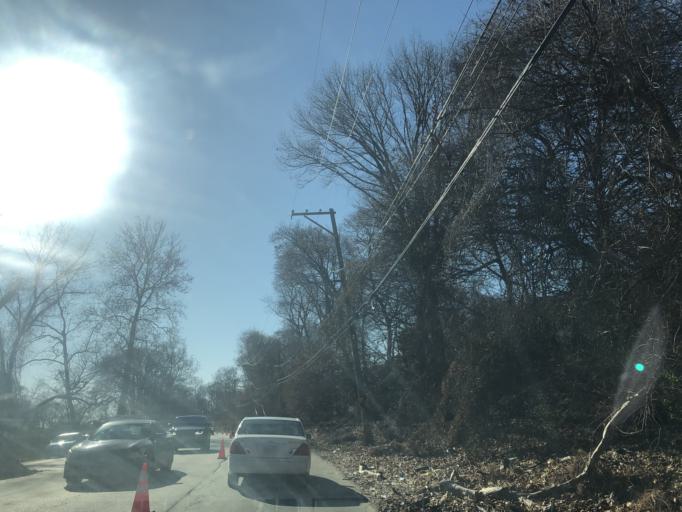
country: US
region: Pennsylvania
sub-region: Montgomery County
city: Bala-Cynwyd
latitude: 39.9872
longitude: -75.2256
